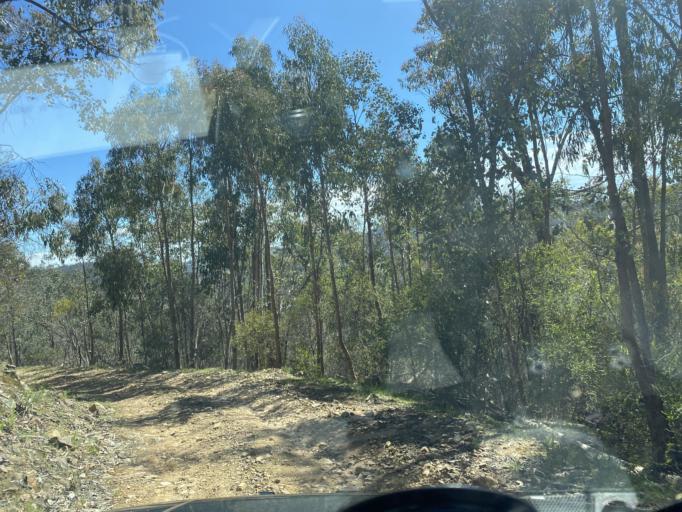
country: AU
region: Victoria
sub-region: Benalla
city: Benalla
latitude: -36.7204
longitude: 146.1825
